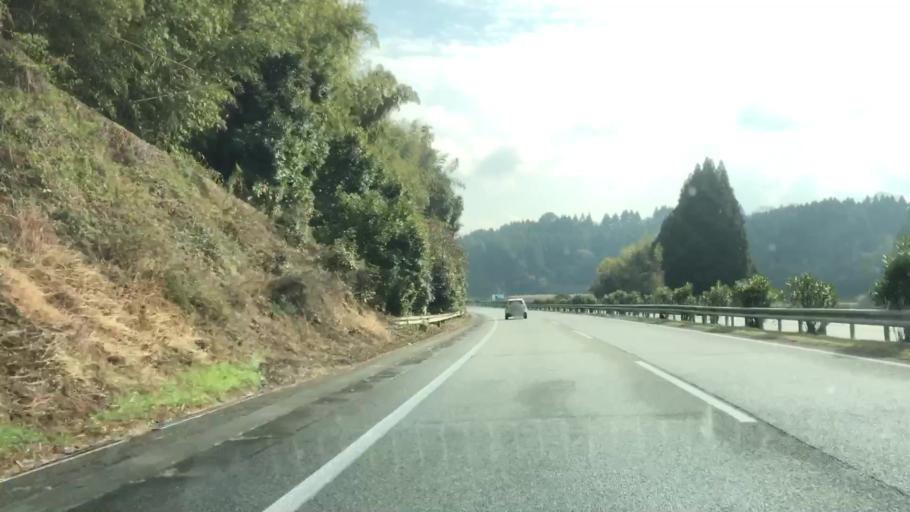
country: JP
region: Kumamoto
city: Yamaga
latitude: 33.0333
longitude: 130.5727
